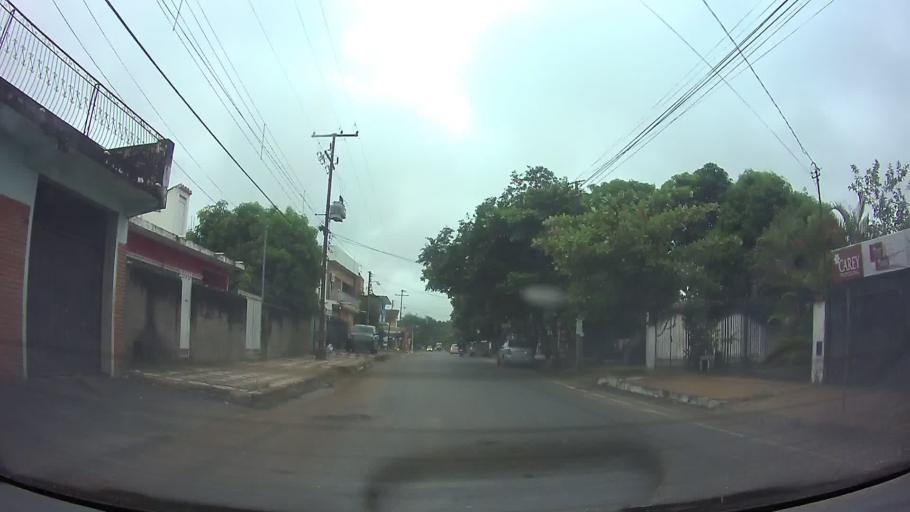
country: PY
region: Central
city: San Lorenzo
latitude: -25.3329
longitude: -57.4994
